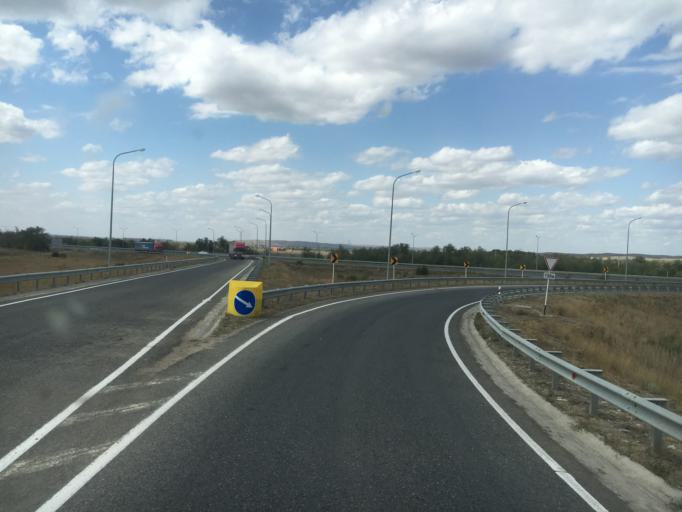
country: KZ
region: Aqtoebe
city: Aqtobe
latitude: 50.2926
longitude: 57.4348
